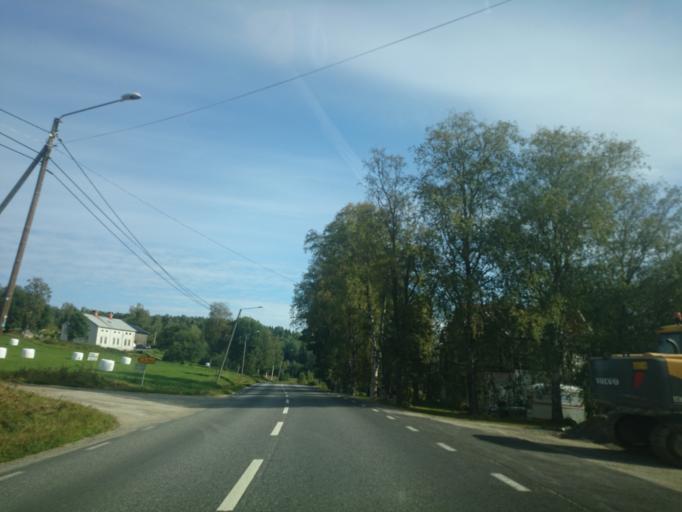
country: SE
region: Vaesternorrland
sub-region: Kramfors Kommun
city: Nordingra
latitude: 62.9365
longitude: 18.2372
